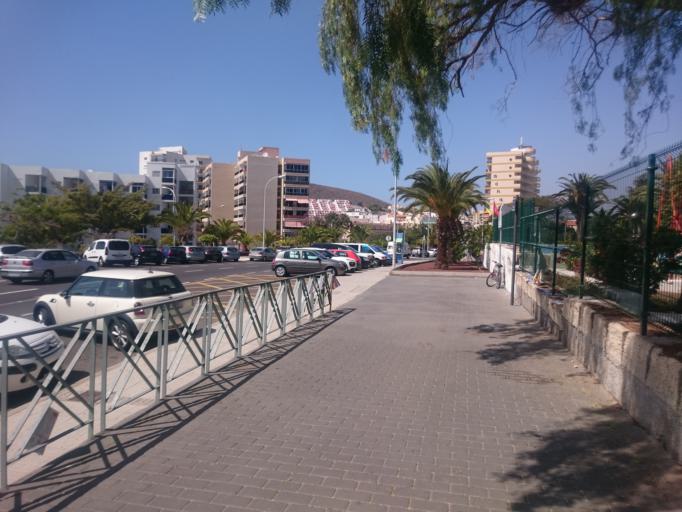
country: ES
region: Canary Islands
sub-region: Provincia de Santa Cruz de Tenerife
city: Playa de las Americas
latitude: 28.0504
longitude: -16.7125
